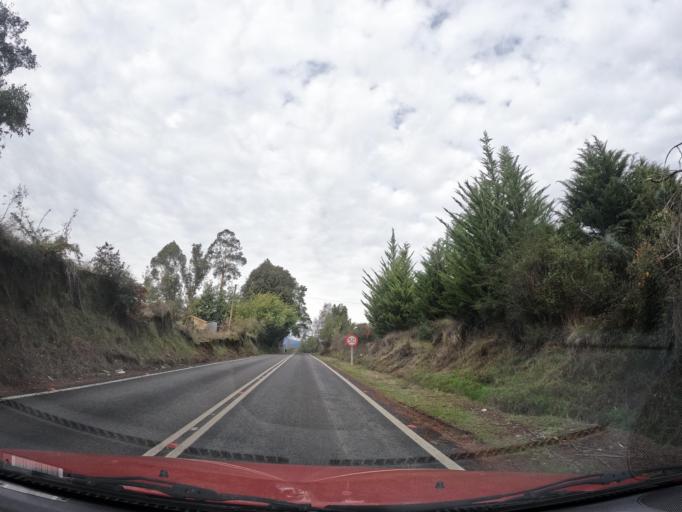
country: CL
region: Maule
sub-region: Provincia de Linares
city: Linares
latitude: -35.9269
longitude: -71.4351
